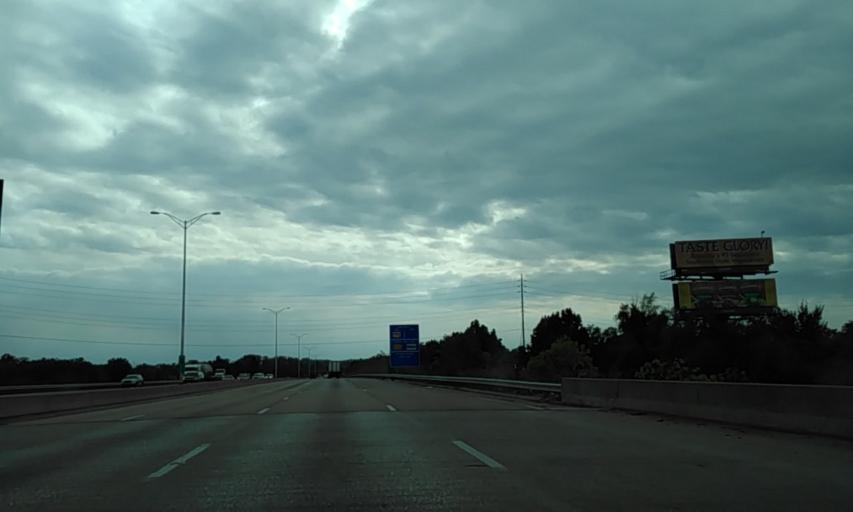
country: US
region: Illinois
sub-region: Saint Clair County
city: Washington Park
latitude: 38.6026
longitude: -90.0857
